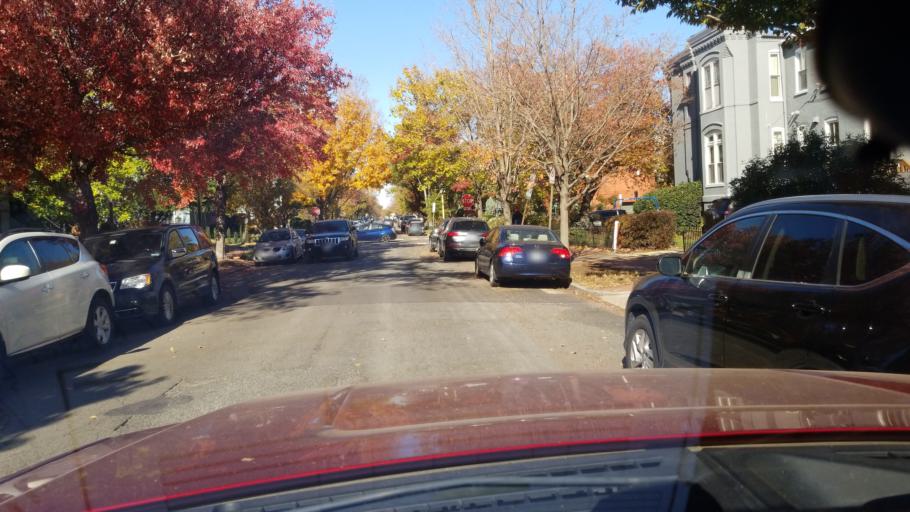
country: US
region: Washington, D.C.
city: Washington, D.C.
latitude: 38.8915
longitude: -76.9902
